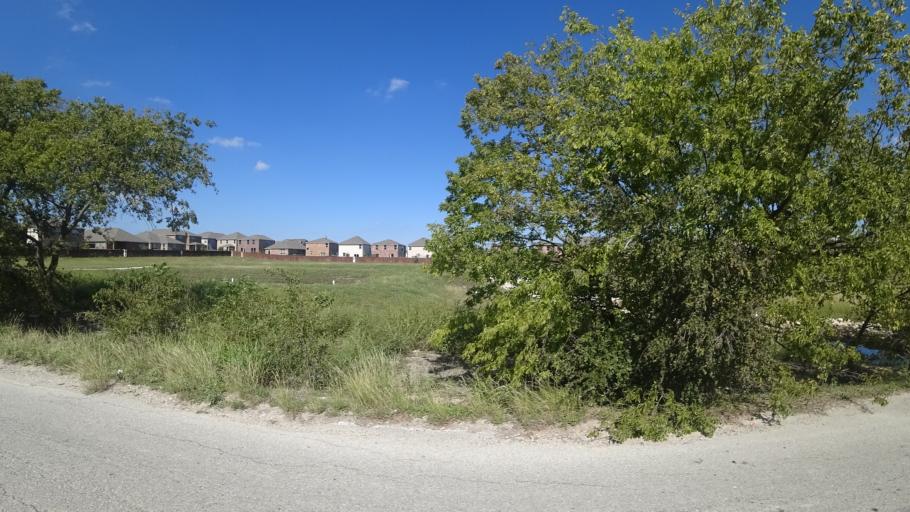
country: US
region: Texas
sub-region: Travis County
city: Manor
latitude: 30.3461
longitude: -97.6221
